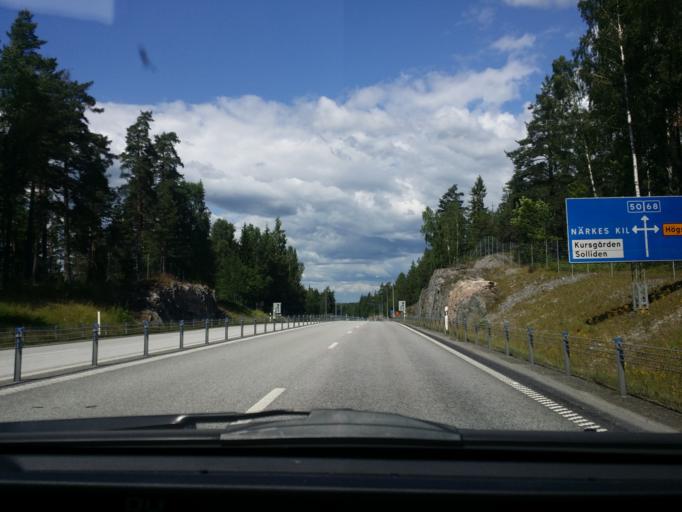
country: SE
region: OErebro
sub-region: Orebro Kommun
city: Hovsta
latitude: 59.3812
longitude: 15.2178
